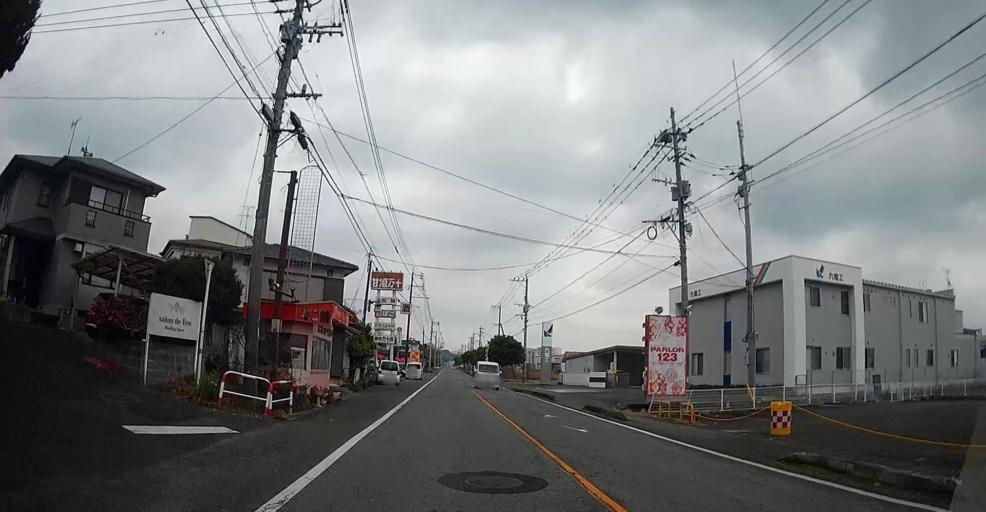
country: JP
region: Kumamoto
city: Matsubase
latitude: 32.6512
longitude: 130.6908
